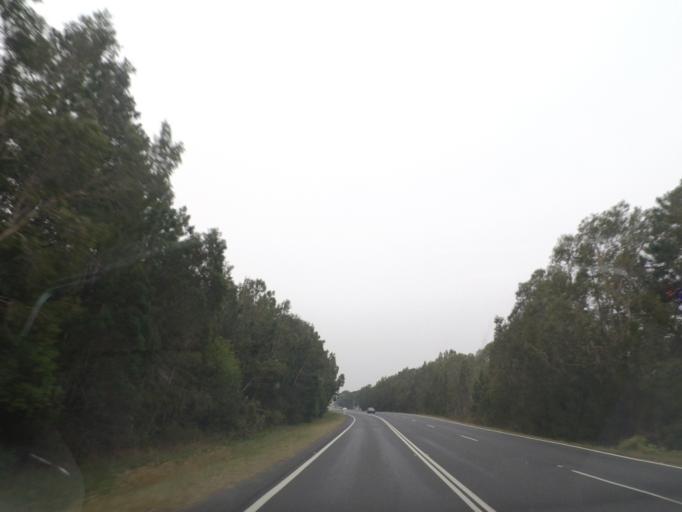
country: AU
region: New South Wales
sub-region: Coffs Harbour
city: Coffs Harbour
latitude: -30.3100
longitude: 153.1185
